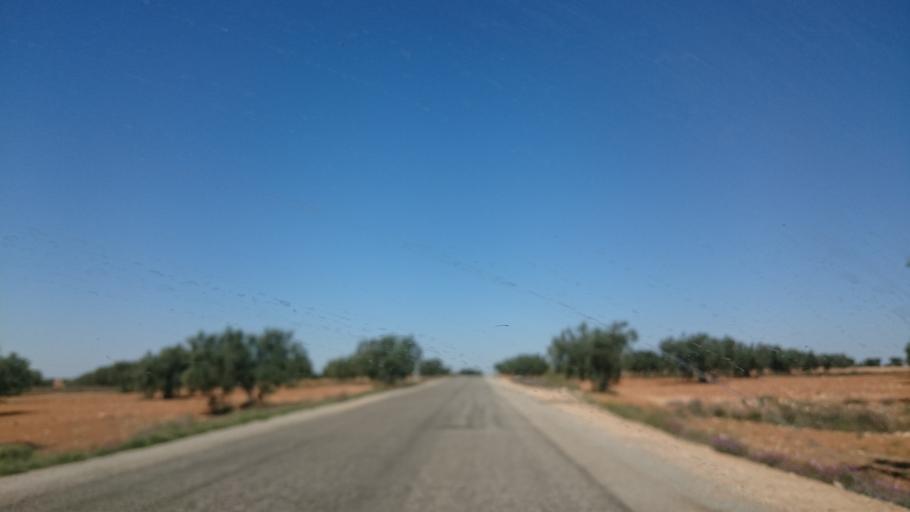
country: TN
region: Safaqis
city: Bi'r `Ali Bin Khalifah
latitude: 34.8646
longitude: 10.4081
